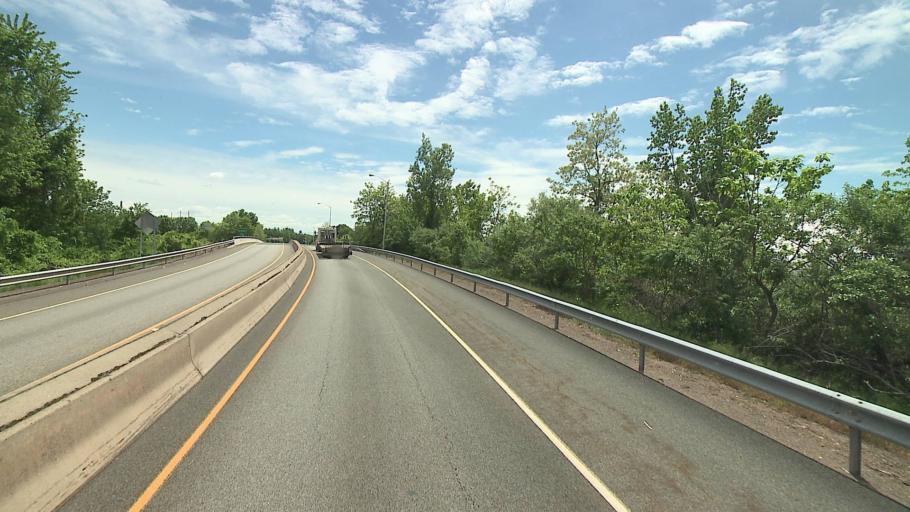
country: US
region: Connecticut
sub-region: Hartford County
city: Windsor Locks
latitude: 41.9211
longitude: -72.6134
